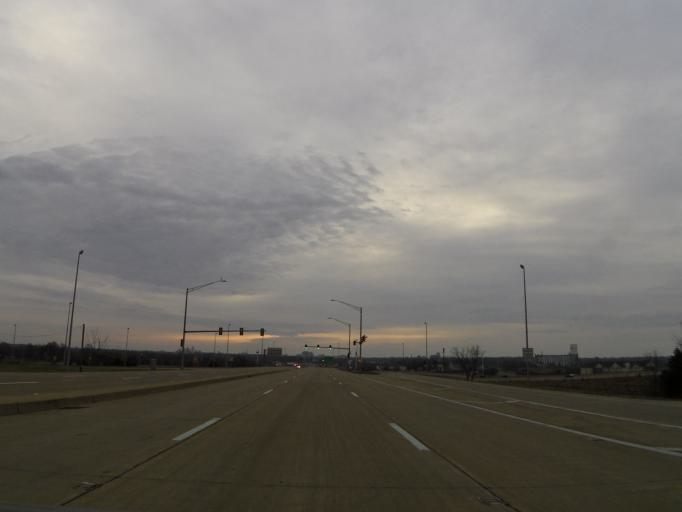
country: US
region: Illinois
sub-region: McLean County
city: Bloomington
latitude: 40.4854
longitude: -89.0325
